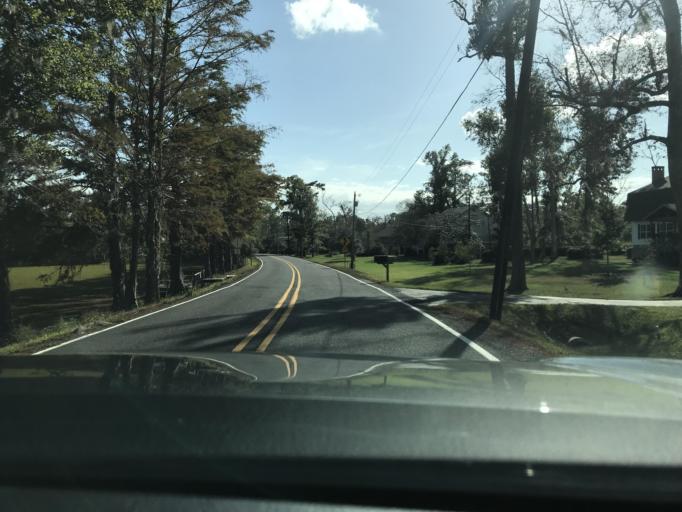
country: US
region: Louisiana
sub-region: Calcasieu Parish
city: Westlake
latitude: 30.3186
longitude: -93.2952
